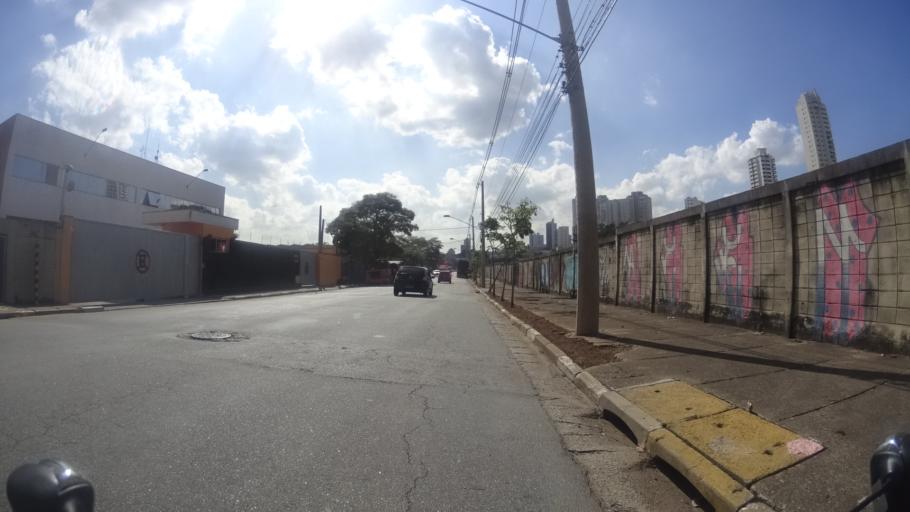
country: BR
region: Sao Paulo
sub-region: Sao Paulo
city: Sao Paulo
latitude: -23.5746
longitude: -46.5945
